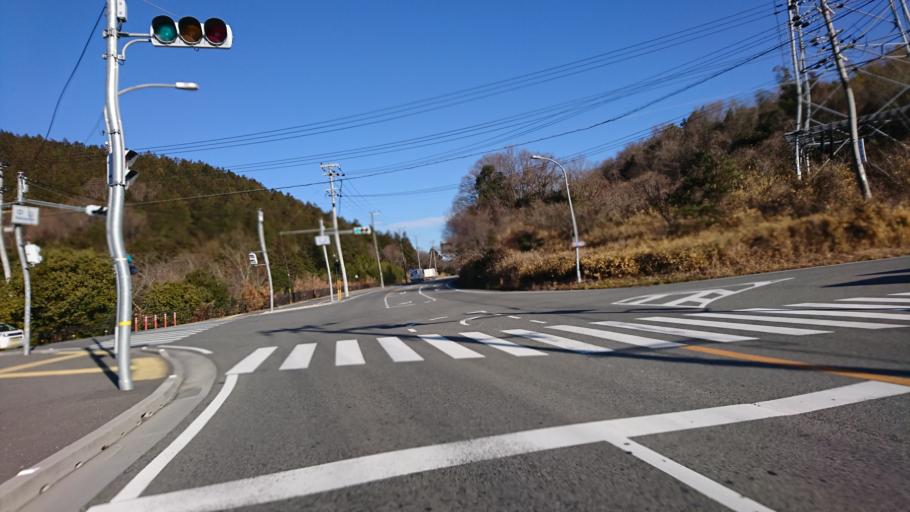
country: JP
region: Hyogo
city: Ono
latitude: 34.8386
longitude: 134.8777
